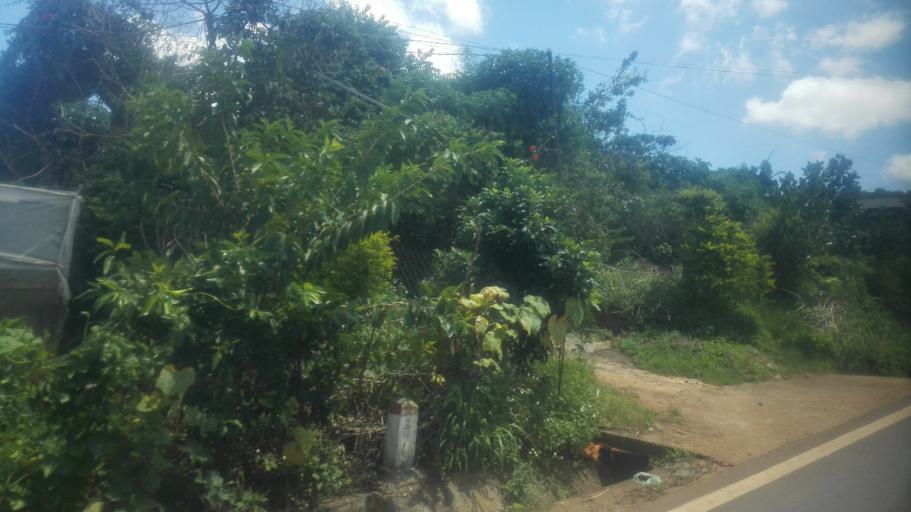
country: VN
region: Lam Dong
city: Da Lat
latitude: 11.9291
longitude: 108.3512
